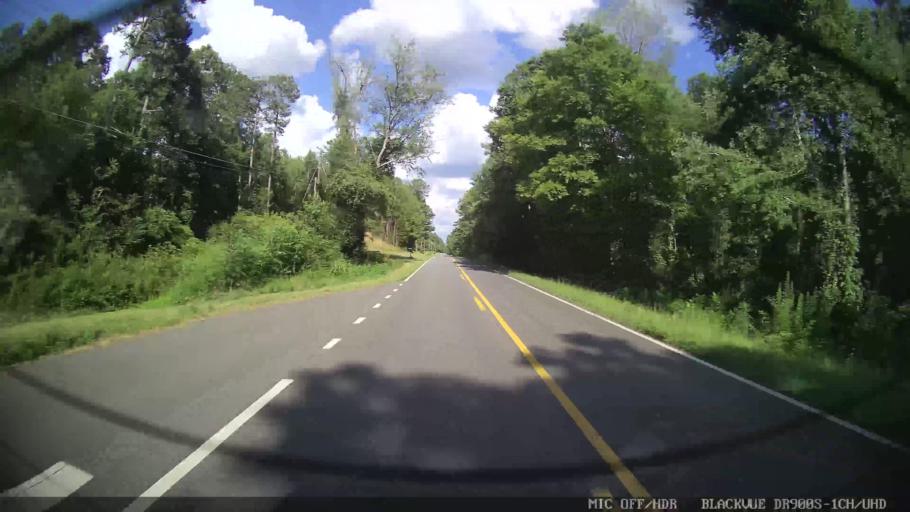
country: US
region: Georgia
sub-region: Bartow County
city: Euharlee
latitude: 34.1766
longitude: -84.9986
